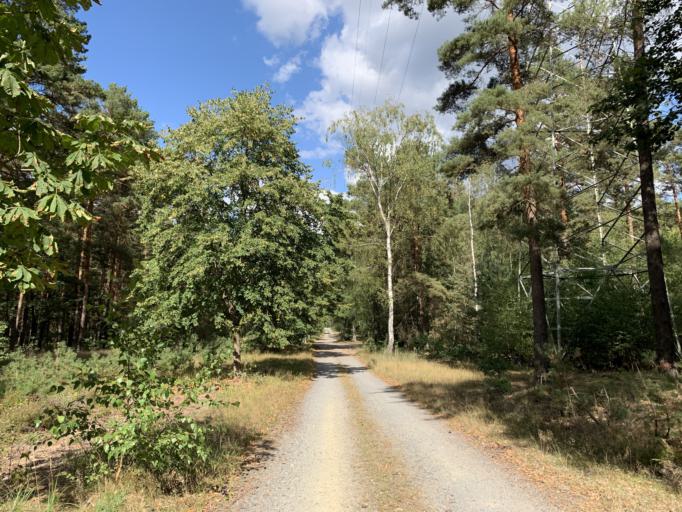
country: DE
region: Brandenburg
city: Michendorf
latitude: 52.3121
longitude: 12.9923
